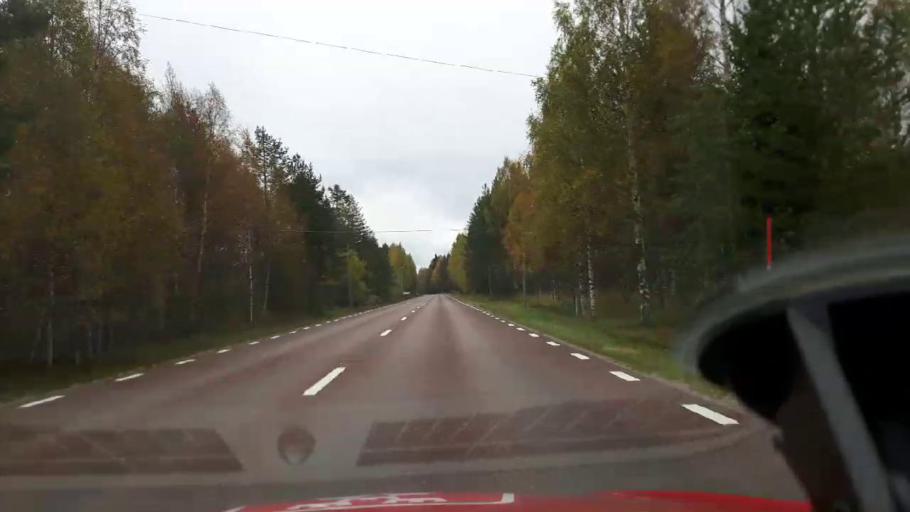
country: SE
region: Jaemtland
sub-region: Harjedalens Kommun
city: Sveg
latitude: 62.3126
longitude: 14.7550
